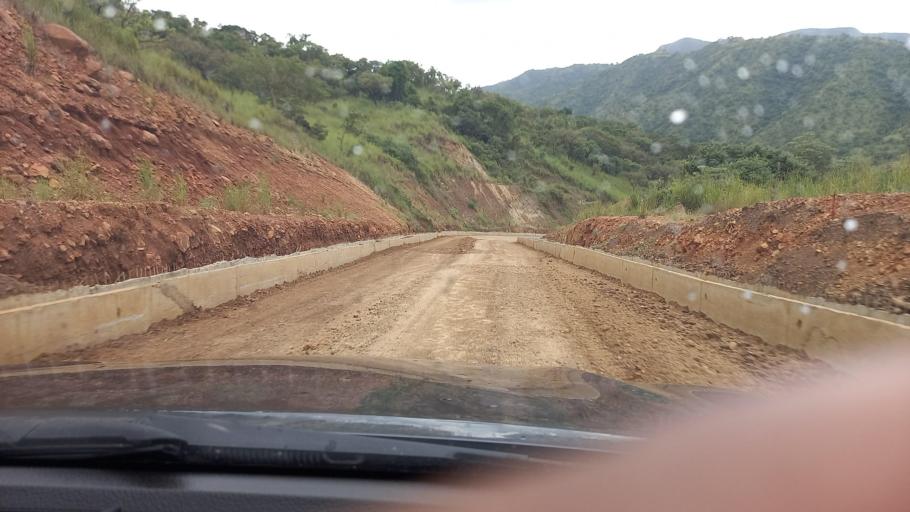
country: ET
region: Southern Nations, Nationalities, and People's Region
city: Mizan Teferi
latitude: 6.1898
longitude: 35.6769
